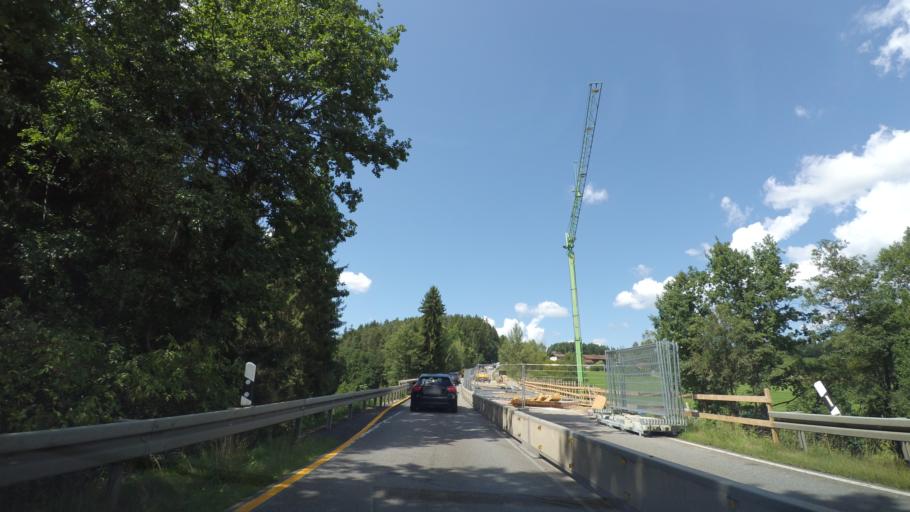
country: DE
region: Bavaria
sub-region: Lower Bavaria
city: Viechtach
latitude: 49.0567
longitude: 12.9130
